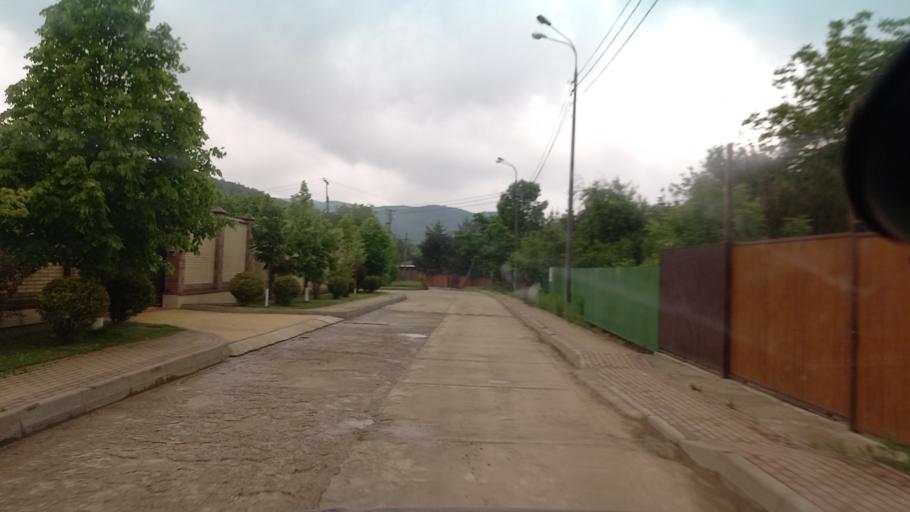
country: RU
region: Krasnodarskiy
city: Azovskaya
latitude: 44.6393
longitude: 38.6163
